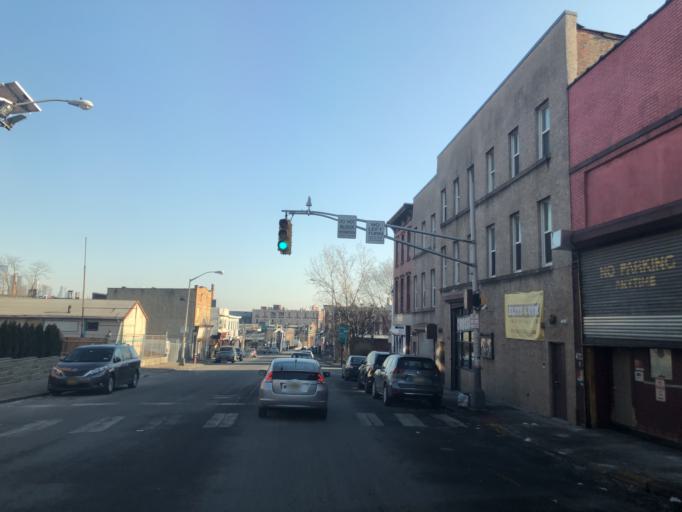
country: US
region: New Jersey
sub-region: Hudson County
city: Jersey City
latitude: 40.7162
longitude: -74.0696
